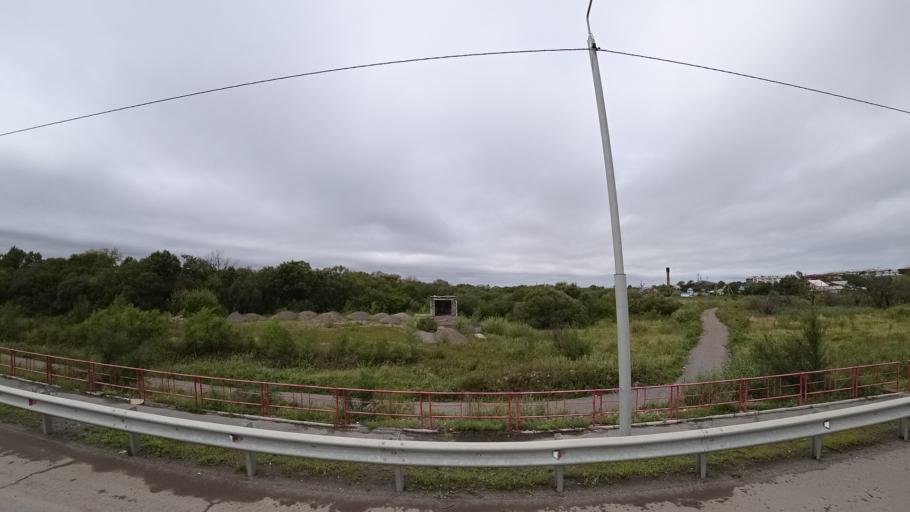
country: RU
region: Primorskiy
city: Monastyrishche
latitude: 44.1981
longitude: 132.4468
